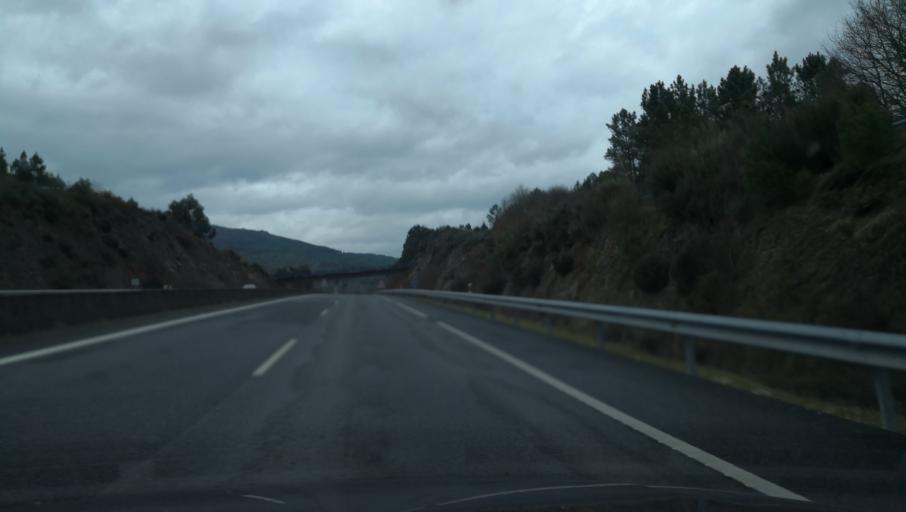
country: ES
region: Galicia
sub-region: Provincia de Ourense
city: Pinor
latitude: 42.4882
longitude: -8.0229
